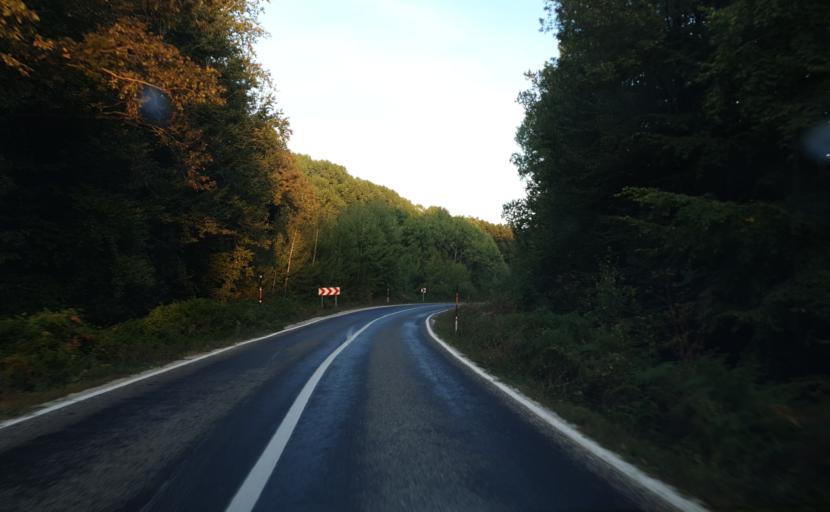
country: TR
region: Kirklareli
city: Igneada
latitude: 41.8756
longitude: 27.8276
